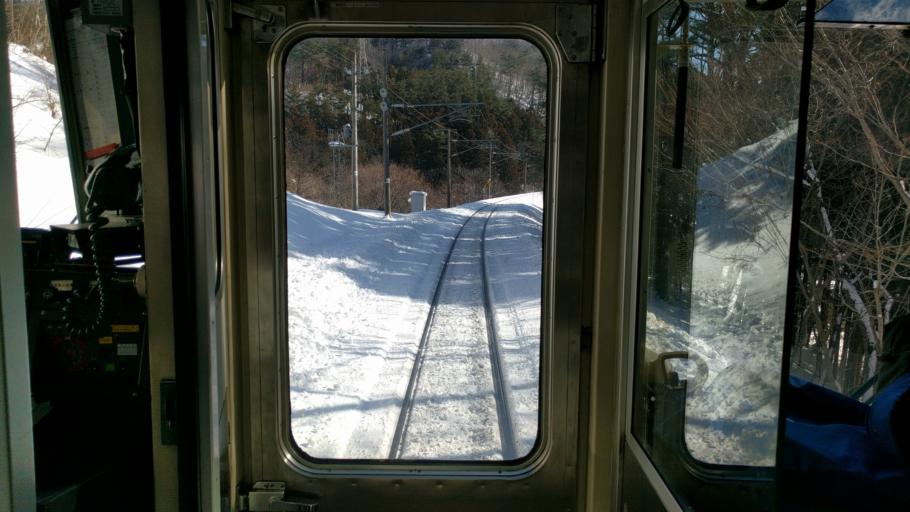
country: JP
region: Fukushima
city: Inawashiro
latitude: 37.4961
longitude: 140.2109
